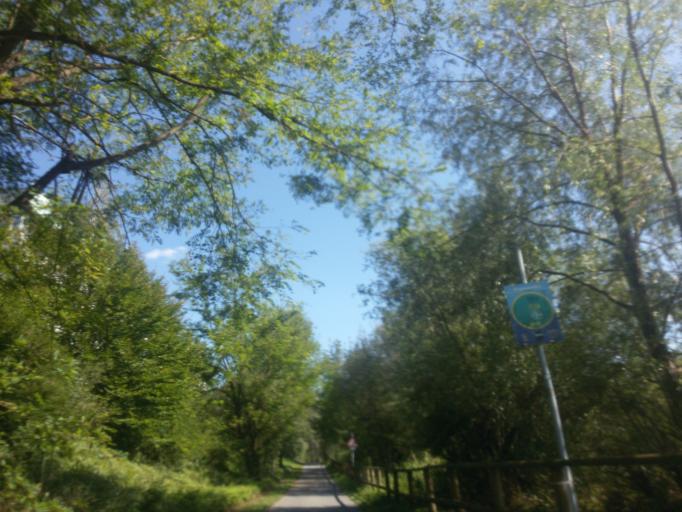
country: AT
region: Carinthia
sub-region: Villach Stadt
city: Villach
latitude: 46.6116
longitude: 13.8824
